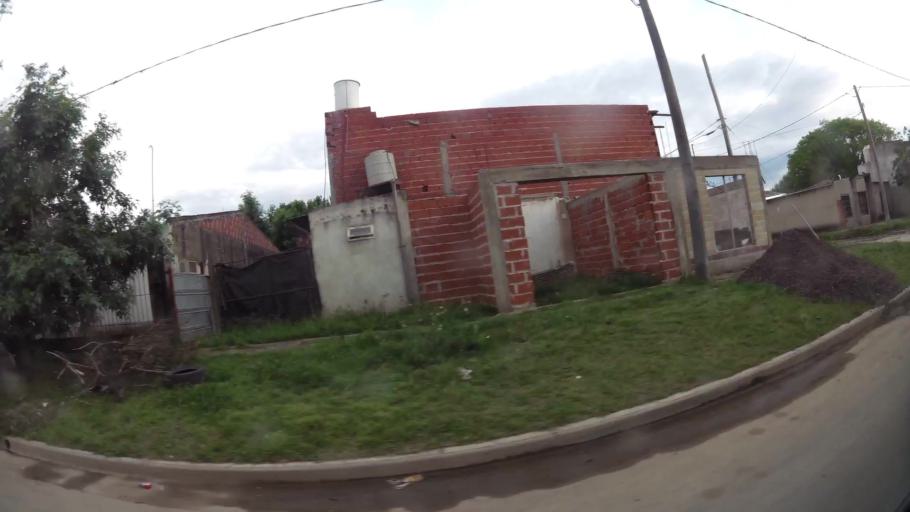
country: AR
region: Buenos Aires
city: San Nicolas de los Arroyos
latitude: -33.3182
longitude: -60.2407
